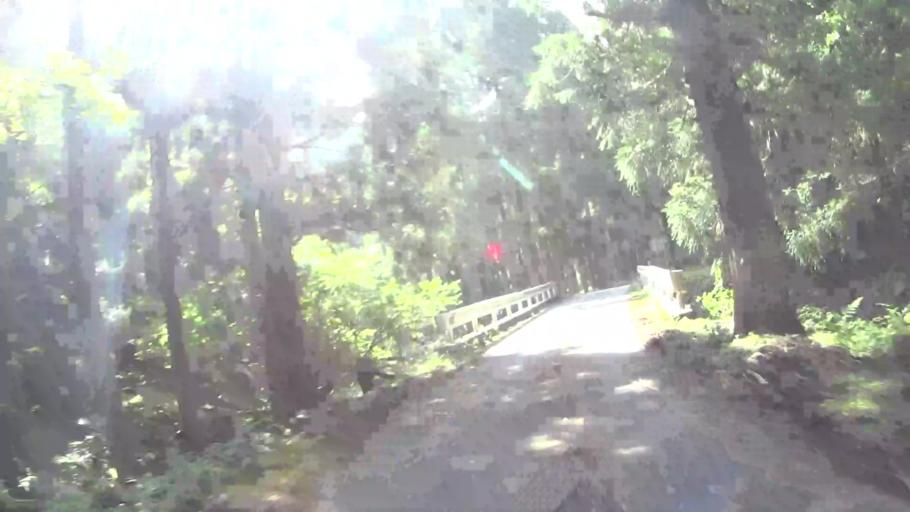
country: JP
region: Fukui
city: Obama
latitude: 35.2936
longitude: 135.6428
